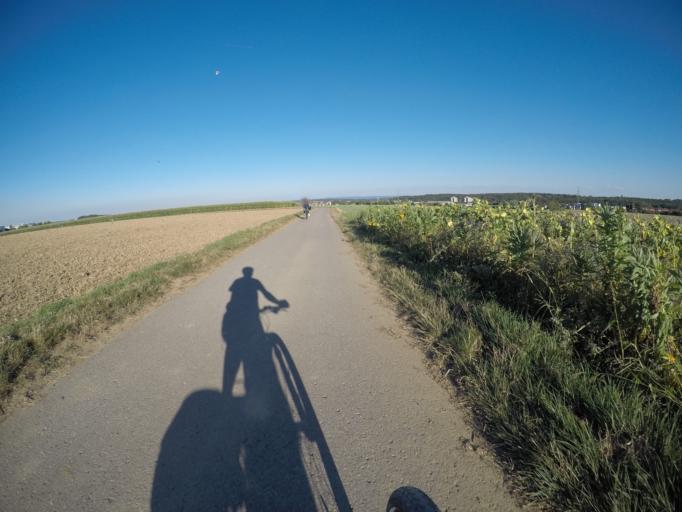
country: DE
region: Baden-Wuerttemberg
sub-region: Regierungsbezirk Stuttgart
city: Holzgerlingen
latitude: 48.6231
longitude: 9.0254
